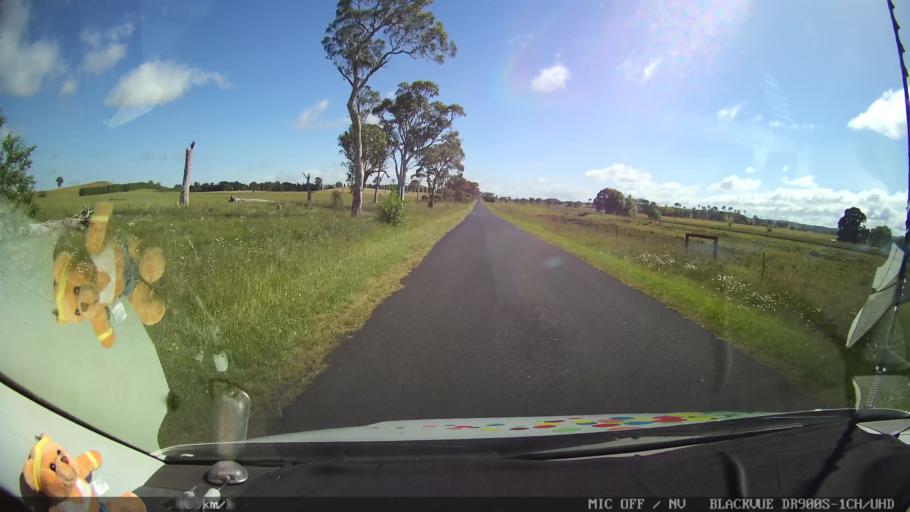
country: AU
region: New South Wales
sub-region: Guyra
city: Guyra
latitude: -30.1830
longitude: 151.6795
